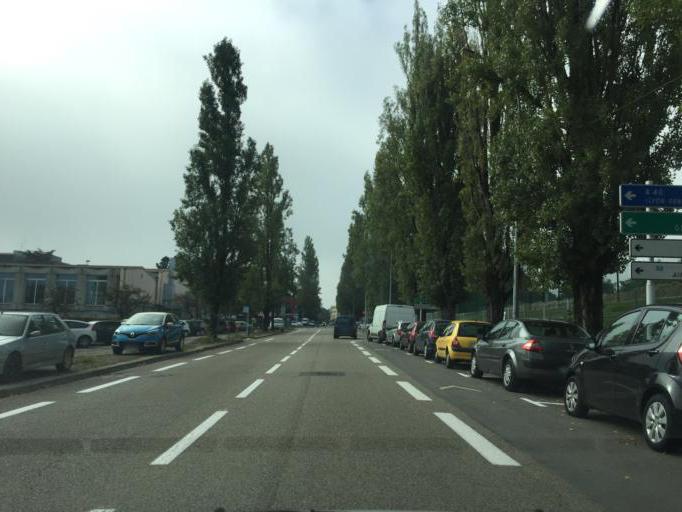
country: FR
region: Rhone-Alpes
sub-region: Departement de l'Ain
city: Bourg-en-Bresse
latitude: 46.1966
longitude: 5.2255
